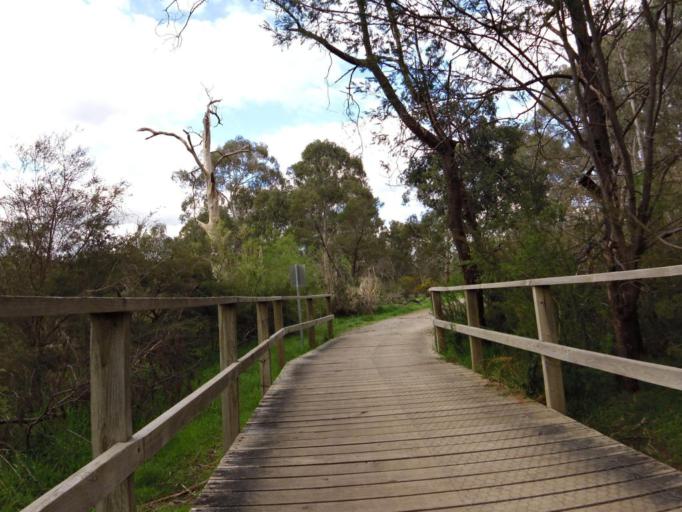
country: AU
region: Victoria
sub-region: Nillumbik
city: Eltham
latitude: -37.7385
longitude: 145.1465
